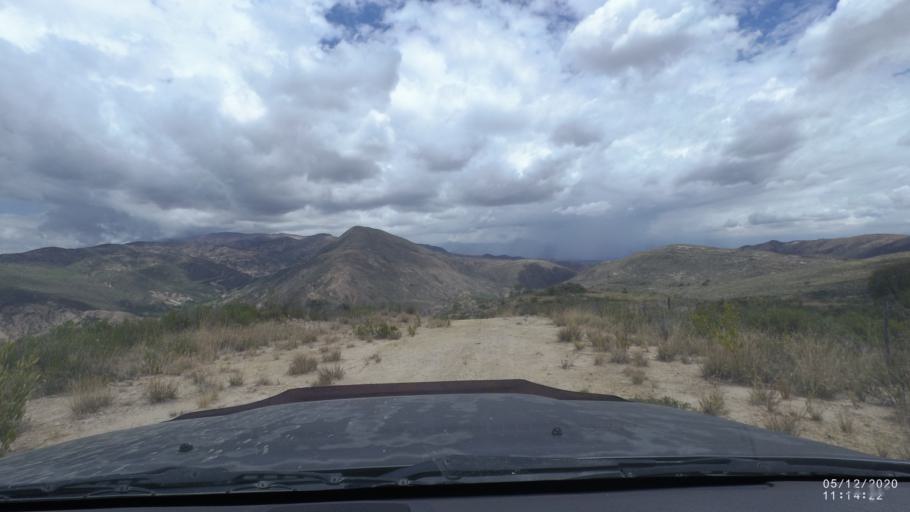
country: BO
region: Cochabamba
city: Sipe Sipe
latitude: -17.5476
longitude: -66.3295
